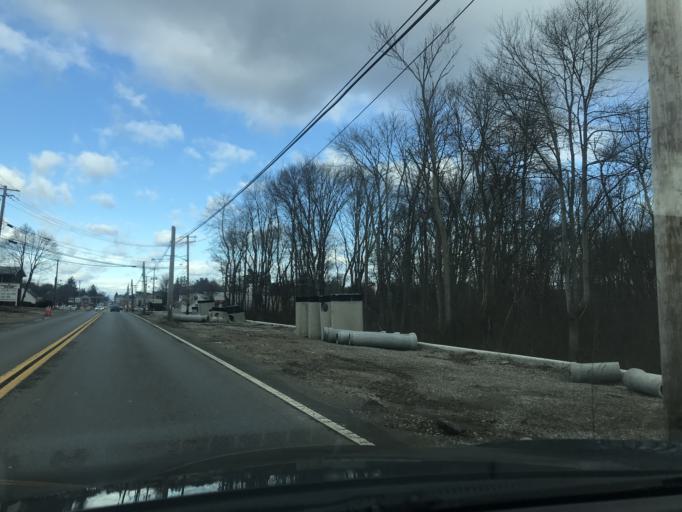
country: US
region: Massachusetts
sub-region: Plymouth County
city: Rockland
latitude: 42.1618
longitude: -70.9552
